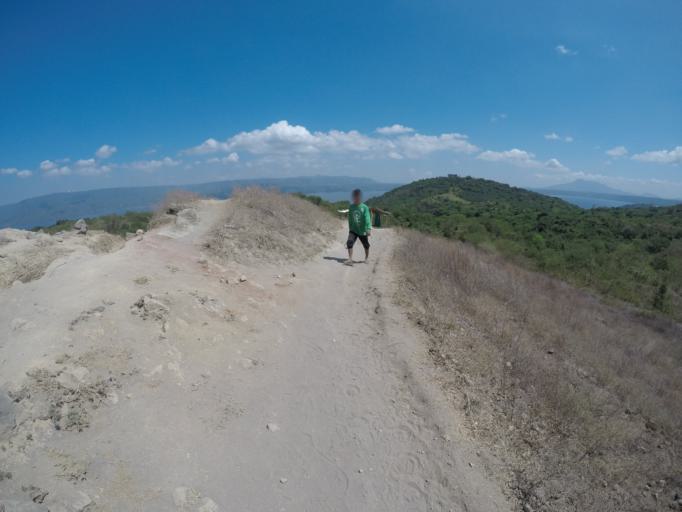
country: PH
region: Calabarzon
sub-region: Province of Batangas
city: Bugaan
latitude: 14.0209
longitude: 120.9994
